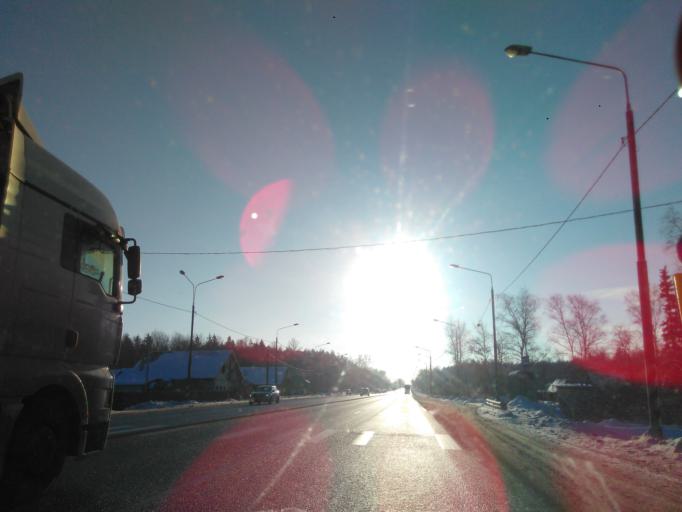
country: RU
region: Moskovskaya
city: Klin
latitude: 56.3820
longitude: 36.6718
